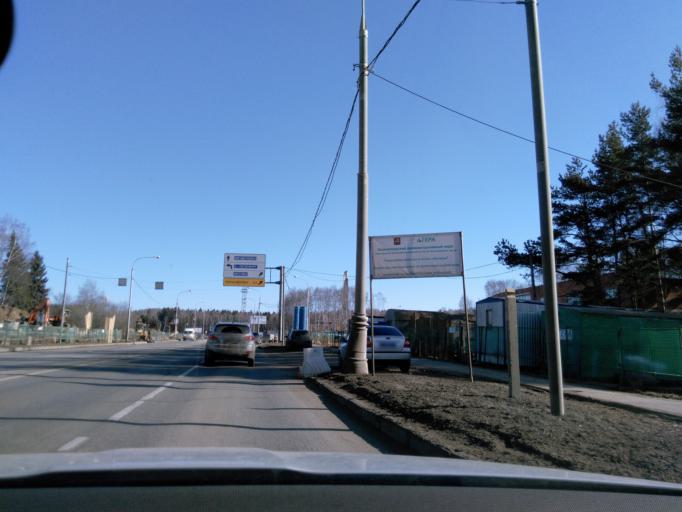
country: RU
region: Moskovskaya
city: Mendeleyevo
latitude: 56.0116
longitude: 37.2044
